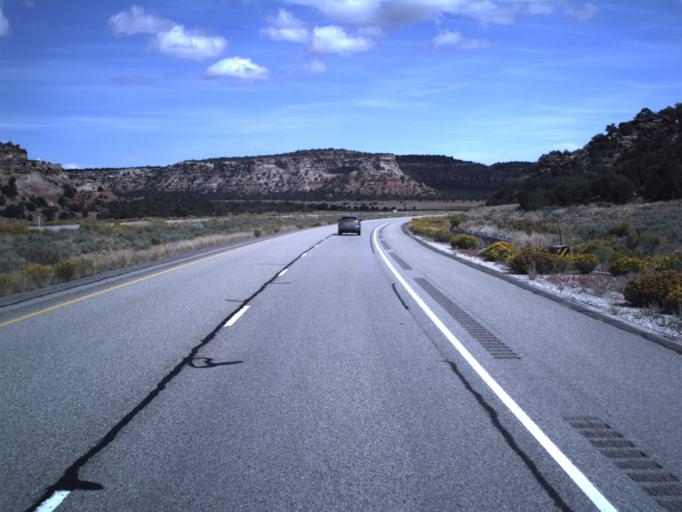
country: US
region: Utah
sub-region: Emery County
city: Castle Dale
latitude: 38.8750
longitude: -110.7484
